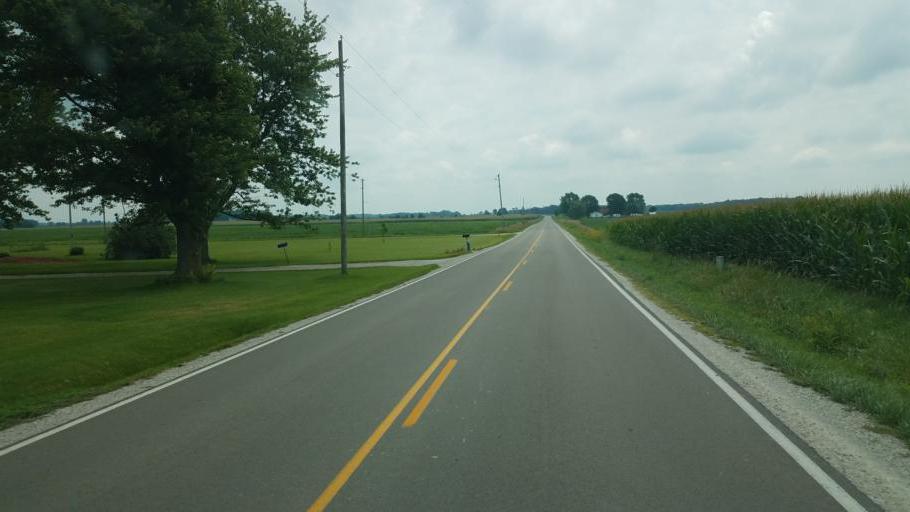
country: US
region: Ohio
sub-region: Crawford County
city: Bucyrus
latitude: 40.7180
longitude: -82.9687
